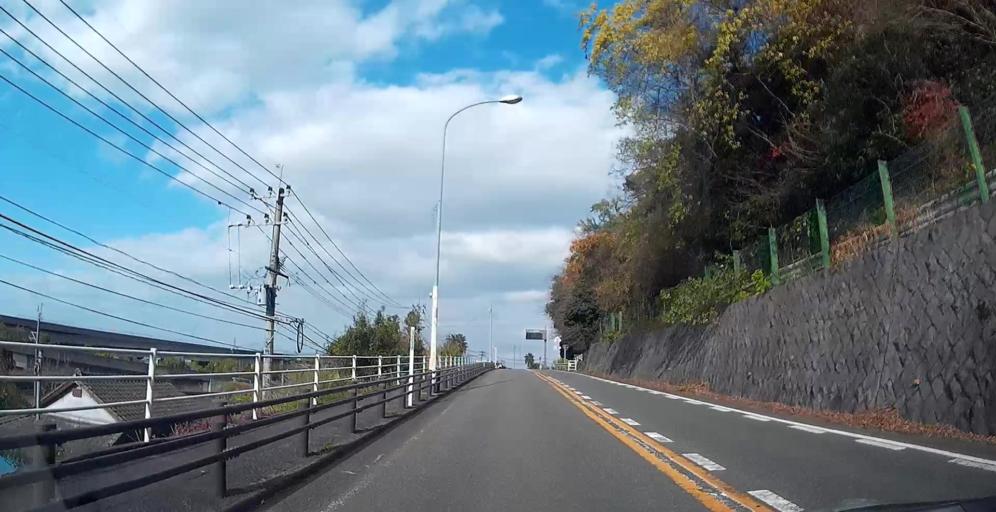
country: JP
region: Kumamoto
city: Yatsushiro
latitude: 32.4284
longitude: 130.5668
